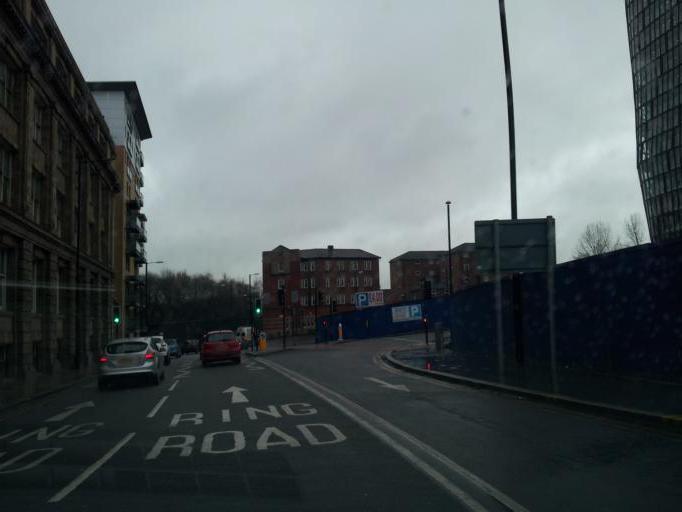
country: GB
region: England
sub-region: Manchester
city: Manchester
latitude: 53.4880
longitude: -2.2397
